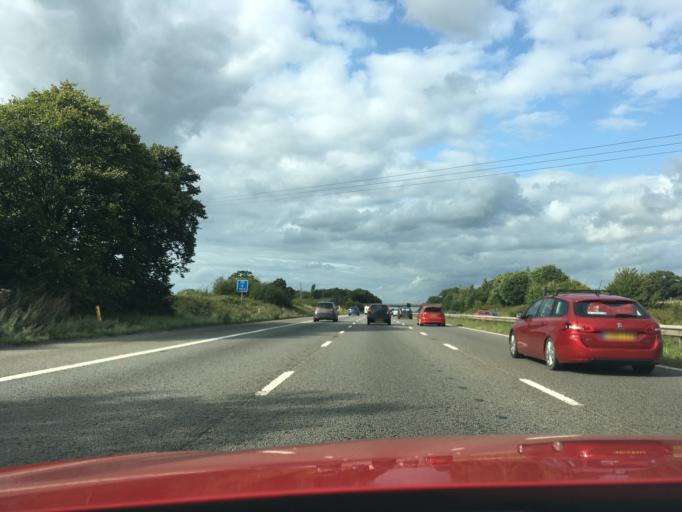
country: GB
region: England
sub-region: Gloucestershire
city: Dursley
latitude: 51.6864
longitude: -2.3993
